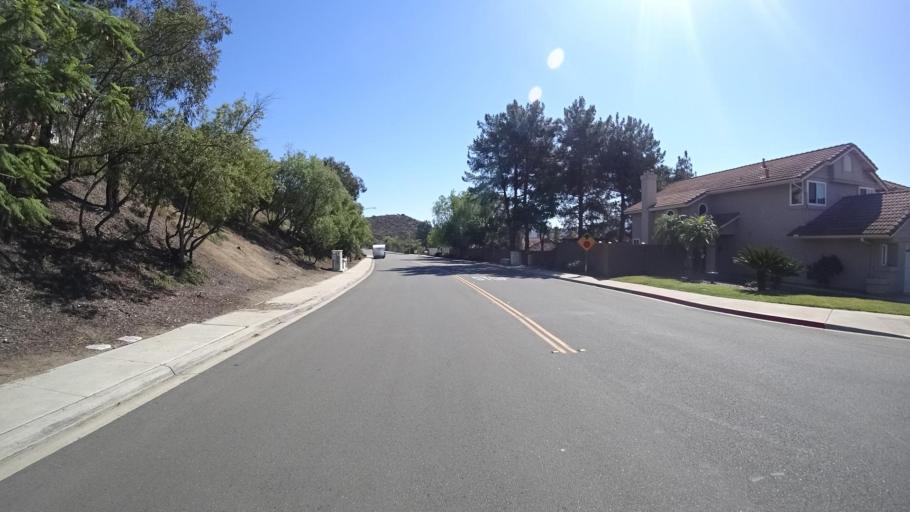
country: US
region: California
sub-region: San Diego County
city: Rancho San Diego
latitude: 32.7557
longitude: -116.9345
